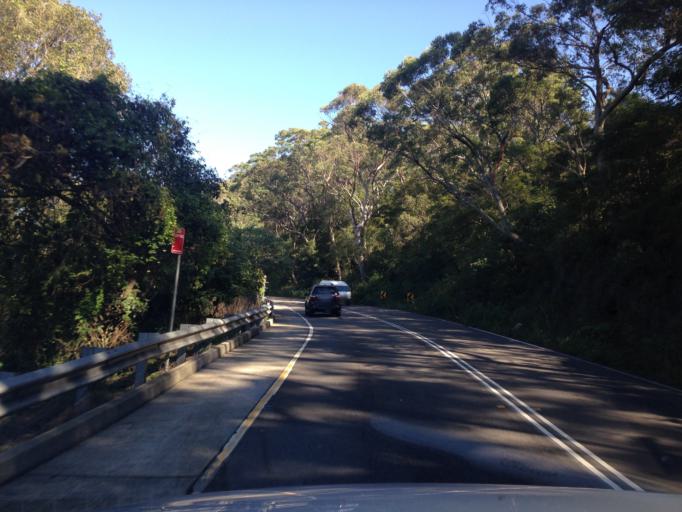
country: AU
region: New South Wales
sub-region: Ku-ring-gai
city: Killara
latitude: -33.7712
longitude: 151.1398
